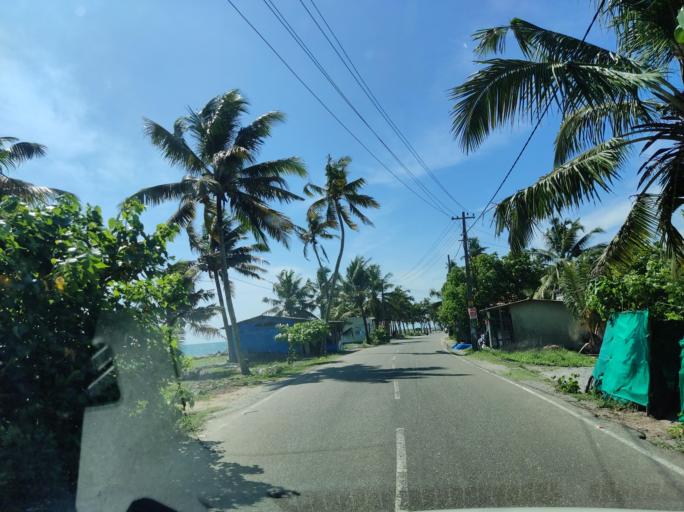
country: IN
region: Kerala
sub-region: Alappuzha
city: Kayankulam
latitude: 9.1997
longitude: 76.4344
